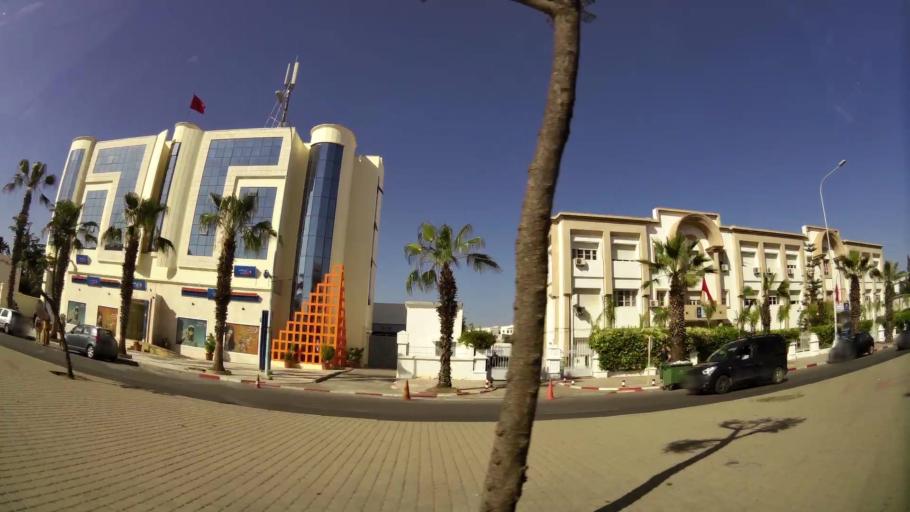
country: MA
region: Oued ed Dahab-Lagouira
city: Dakhla
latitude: 30.4128
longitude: -9.5658
